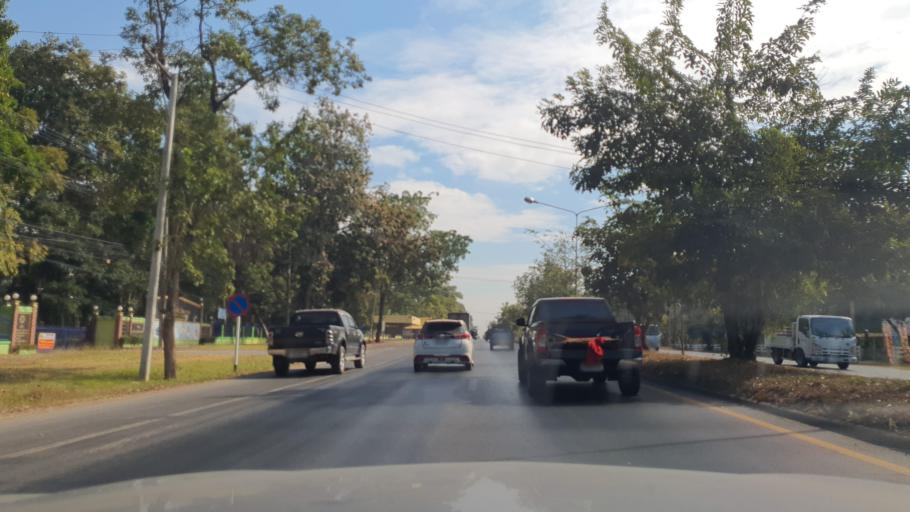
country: TH
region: Kalasin
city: Yang Talat
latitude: 16.4061
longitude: 103.4171
